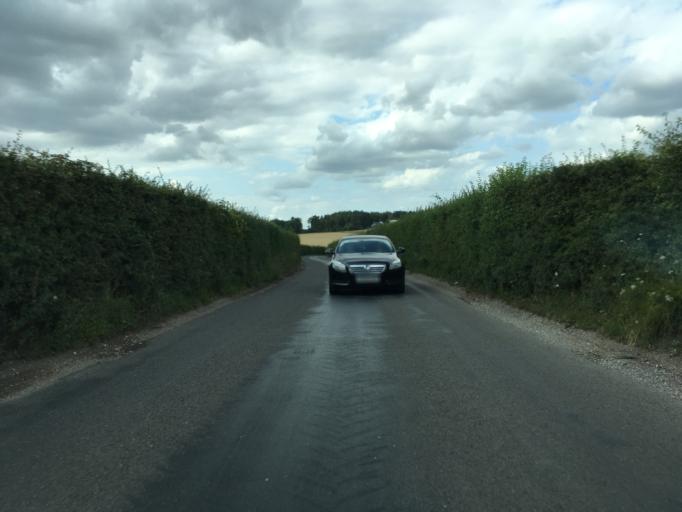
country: GB
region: England
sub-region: Hampshire
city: Overton
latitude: 51.2070
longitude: -1.2620
